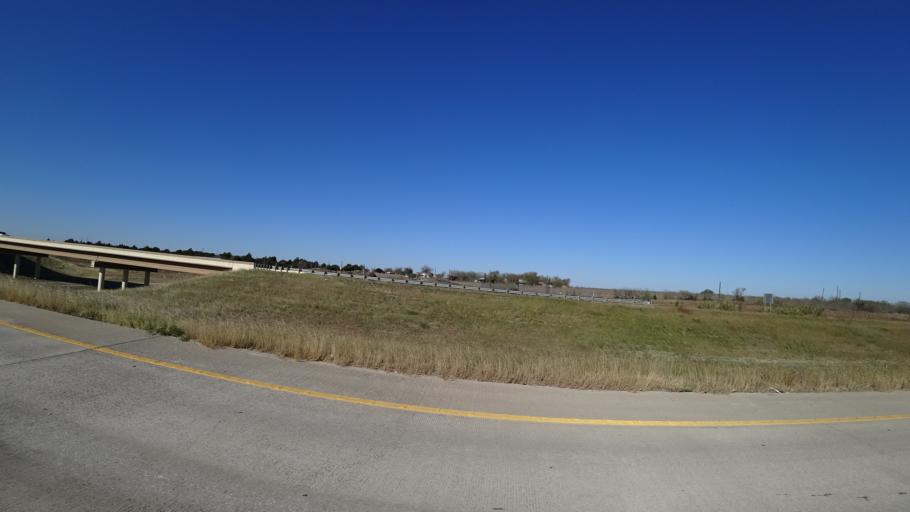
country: US
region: Texas
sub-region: Travis County
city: Onion Creek
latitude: 30.1029
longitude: -97.6685
